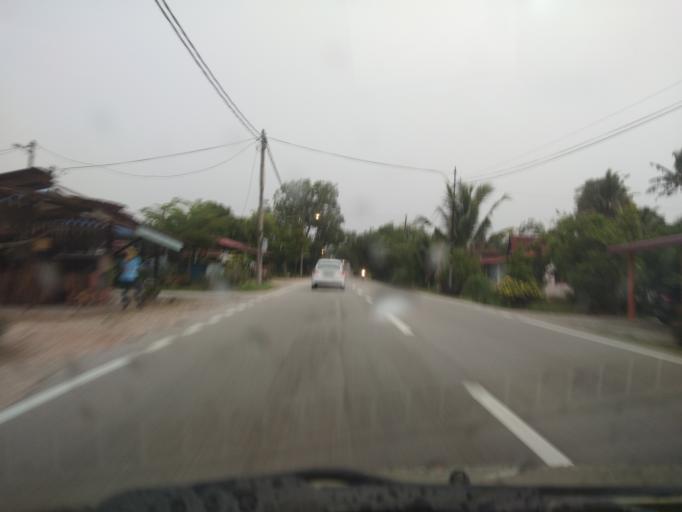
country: MY
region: Penang
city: Permatang Kuching
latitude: 5.4824
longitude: 100.4011
